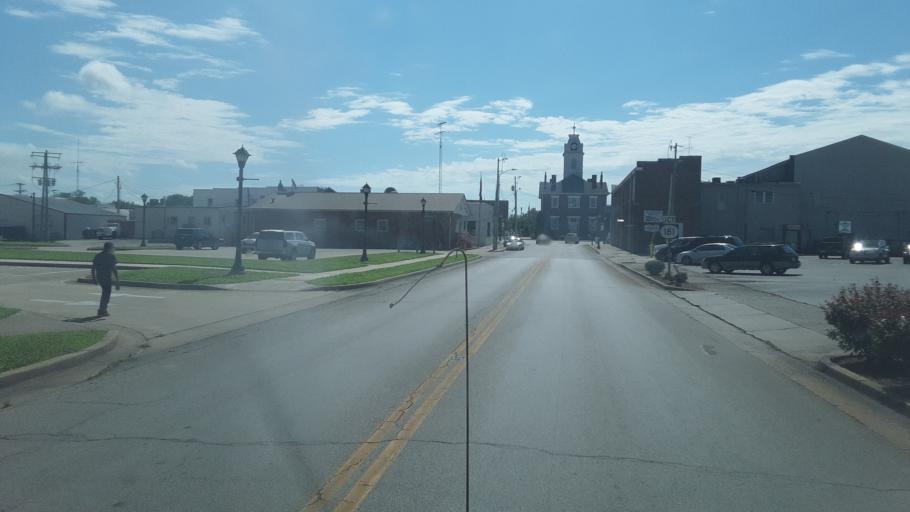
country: US
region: Kentucky
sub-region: Todd County
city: Elkton
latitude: 36.8097
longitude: -87.1560
